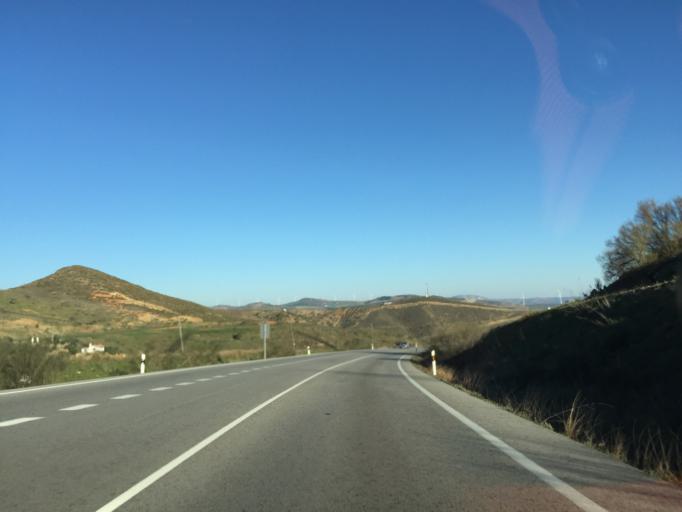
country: ES
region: Andalusia
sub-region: Provincia de Malaga
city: Ardales
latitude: 36.8632
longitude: -4.8412
